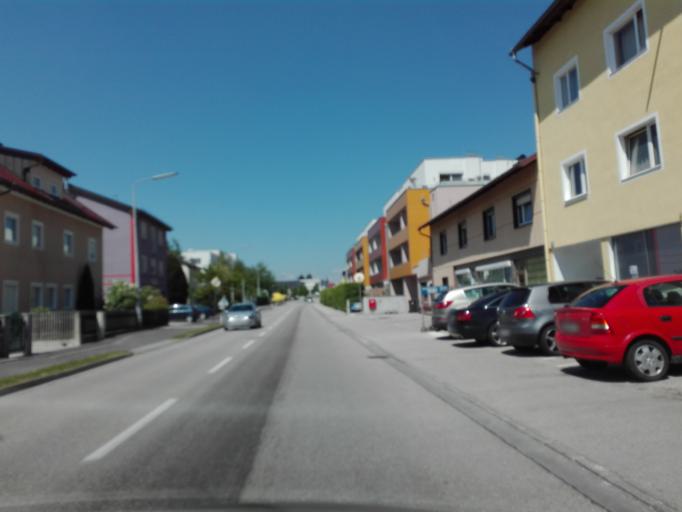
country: AT
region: Upper Austria
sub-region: Politischer Bezirk Linz-Land
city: Traun
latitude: 48.2373
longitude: 14.2637
